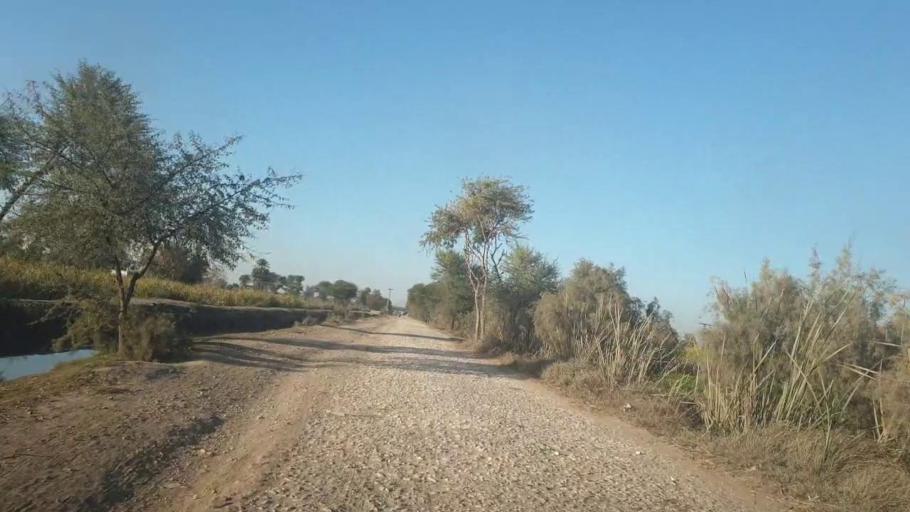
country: PK
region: Sindh
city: Ghotki
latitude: 28.0025
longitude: 69.2704
